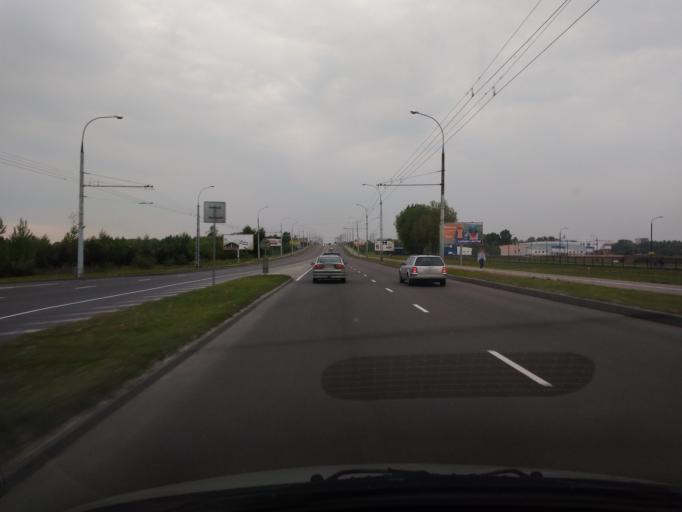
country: BY
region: Brest
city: Brest
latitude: 52.0815
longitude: 23.7376
